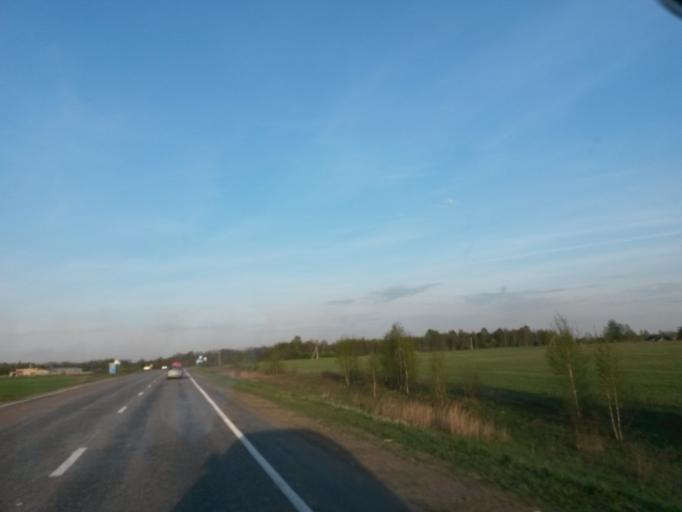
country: RU
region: Jaroslavl
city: Kurba
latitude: 57.6813
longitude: 39.5155
